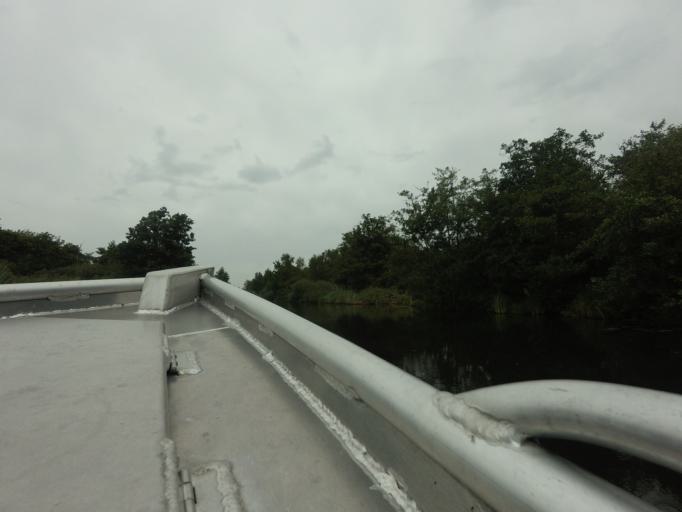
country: NL
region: Overijssel
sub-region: Gemeente Steenwijkerland
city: Sint Jansklooster
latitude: 52.7132
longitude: 6.0377
